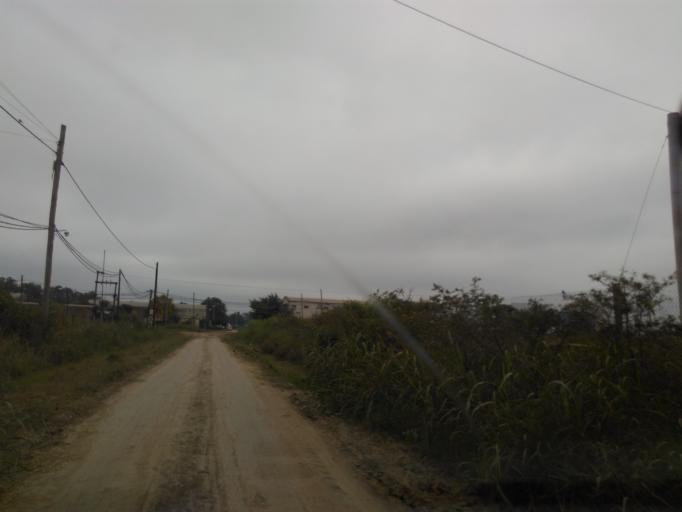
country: AR
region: Chaco
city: Fontana
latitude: -27.4479
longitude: -59.0275
